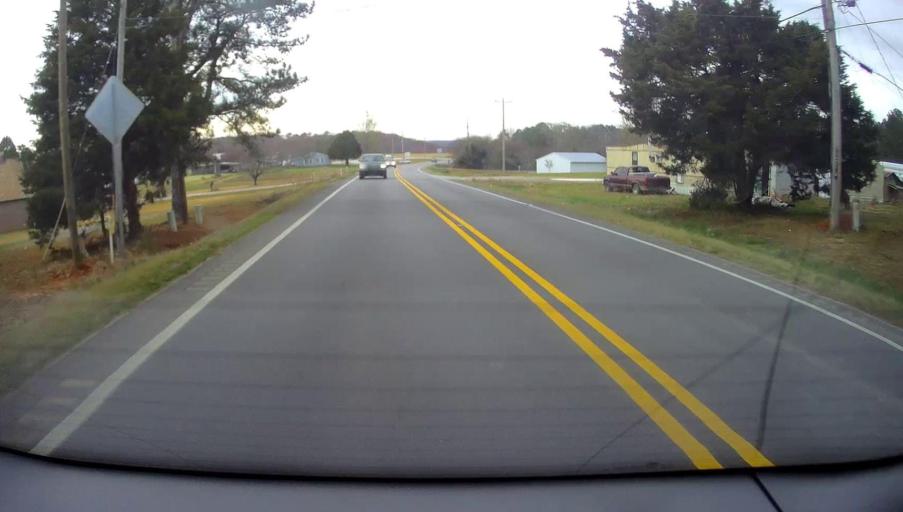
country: US
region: Alabama
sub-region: Morgan County
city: Priceville
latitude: 34.5049
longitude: -86.8664
